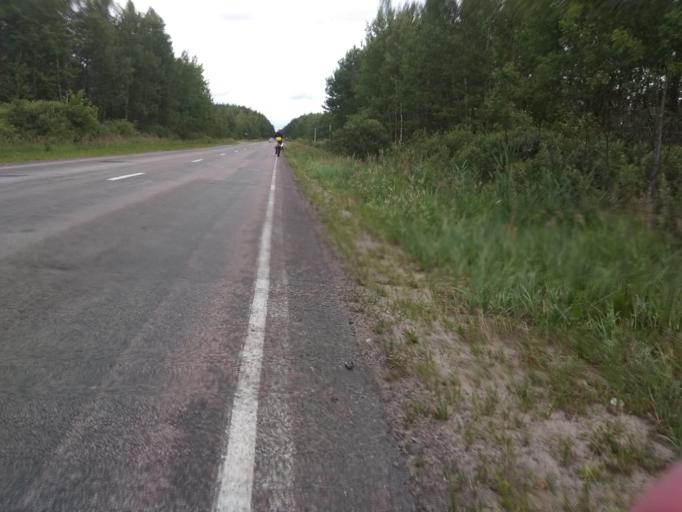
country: RU
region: Moskovskaya
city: Misheronskiy
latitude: 55.6074
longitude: 39.7121
